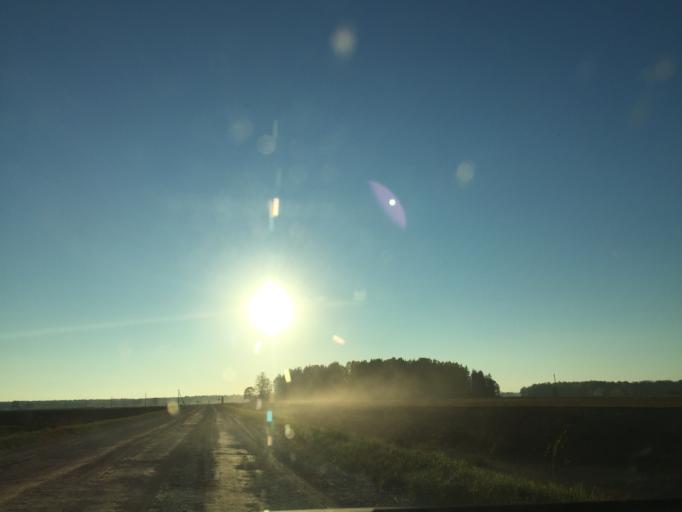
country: LT
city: Vieksniai
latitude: 56.3101
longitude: 22.5472
